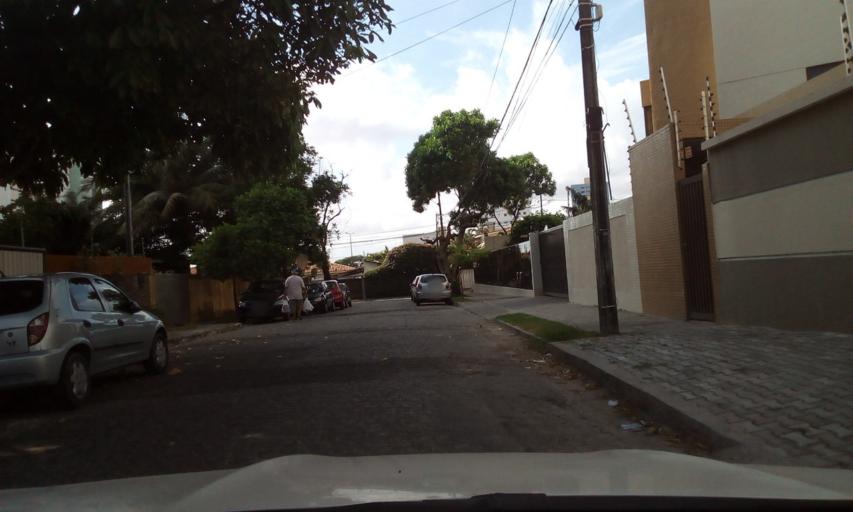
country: BR
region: Paraiba
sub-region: Joao Pessoa
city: Joao Pessoa
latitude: -7.1164
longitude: -34.8401
